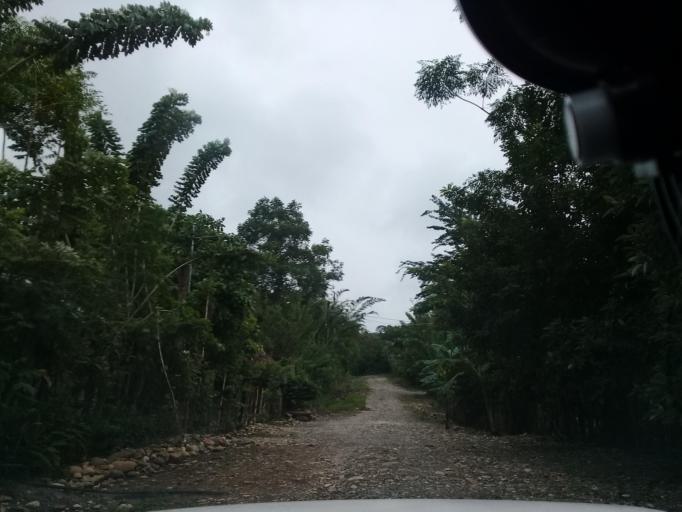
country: MX
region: Veracruz
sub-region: Chalma
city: San Pedro Coyutla
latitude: 21.2227
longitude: -98.4268
